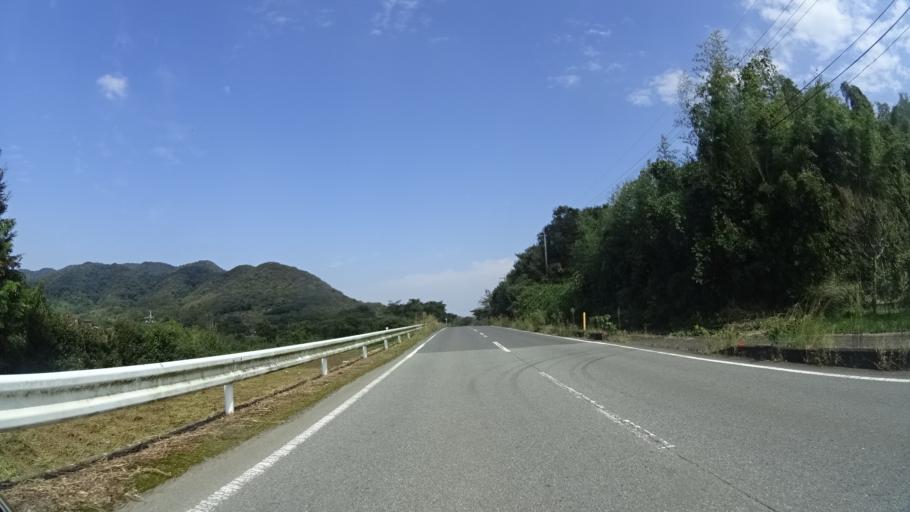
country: JP
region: Kumamoto
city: Uto
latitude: 32.6703
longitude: 130.7190
